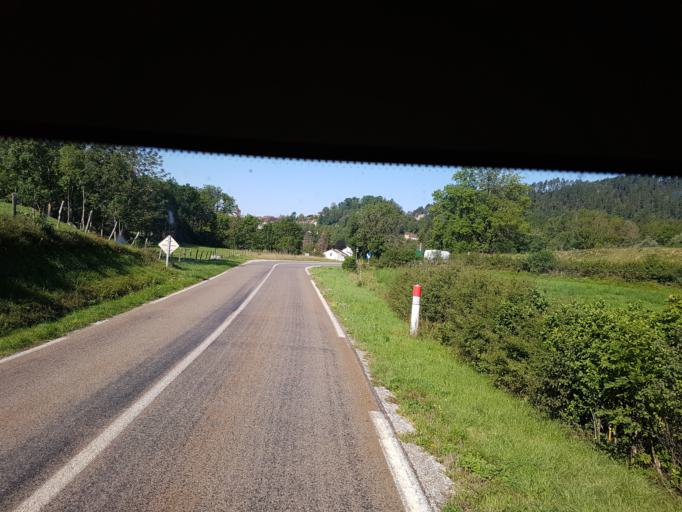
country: FR
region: Franche-Comte
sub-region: Departement du Jura
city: Orgelet
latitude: 46.5236
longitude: 5.6254
